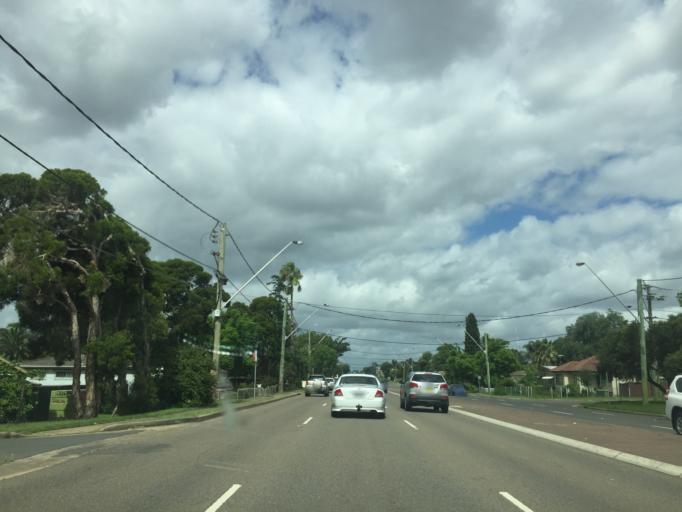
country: AU
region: New South Wales
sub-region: Blacktown
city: Mount Druitt
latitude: -33.7737
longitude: 150.7895
